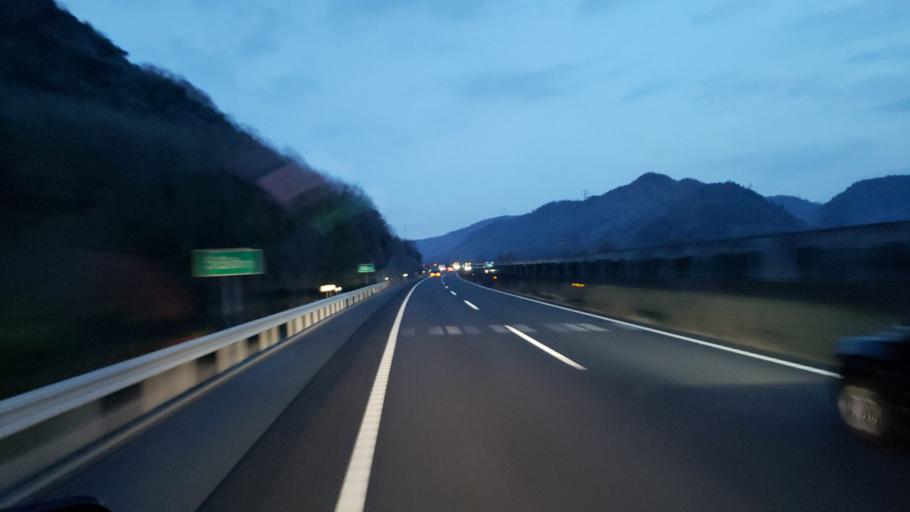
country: JP
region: Hyogo
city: Kakogawacho-honmachi
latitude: 34.8531
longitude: 134.7878
